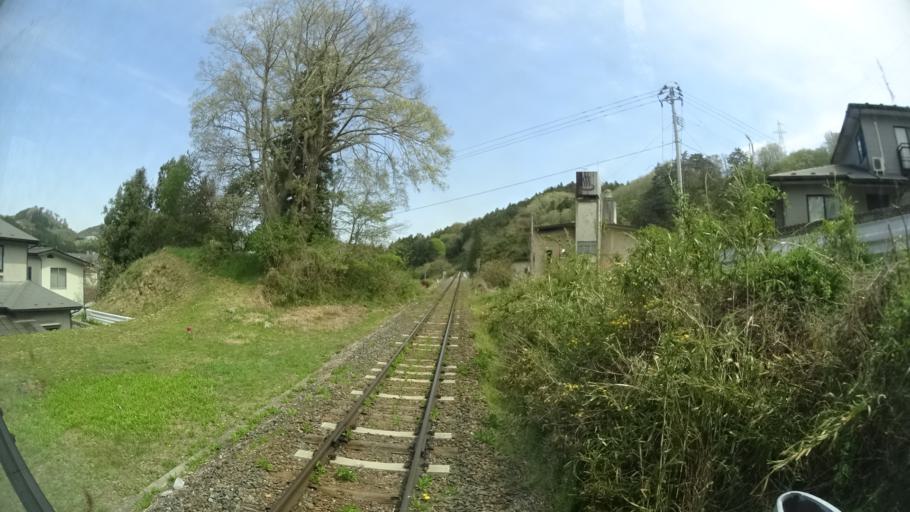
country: JP
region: Iwate
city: Ichinoseki
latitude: 38.9898
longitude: 141.2543
